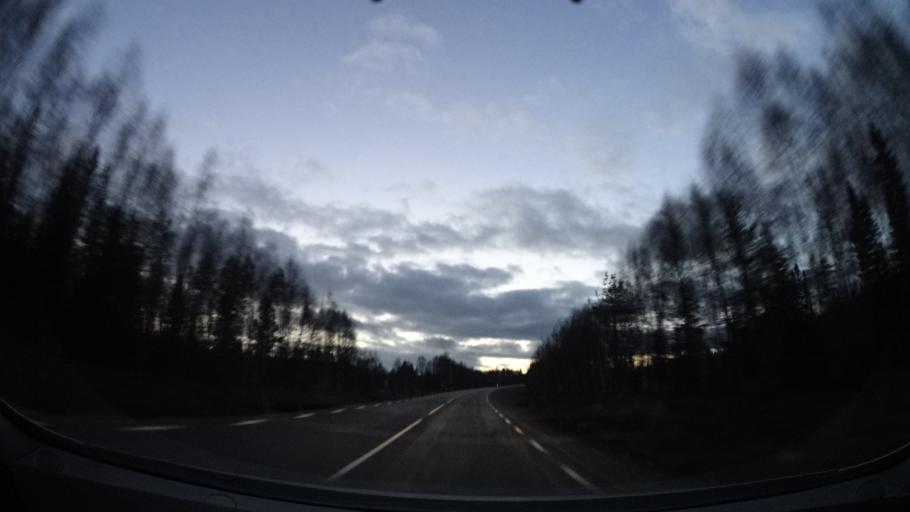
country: SE
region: Vaesterbotten
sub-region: Asele Kommun
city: Asele
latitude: 64.2049
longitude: 16.9621
